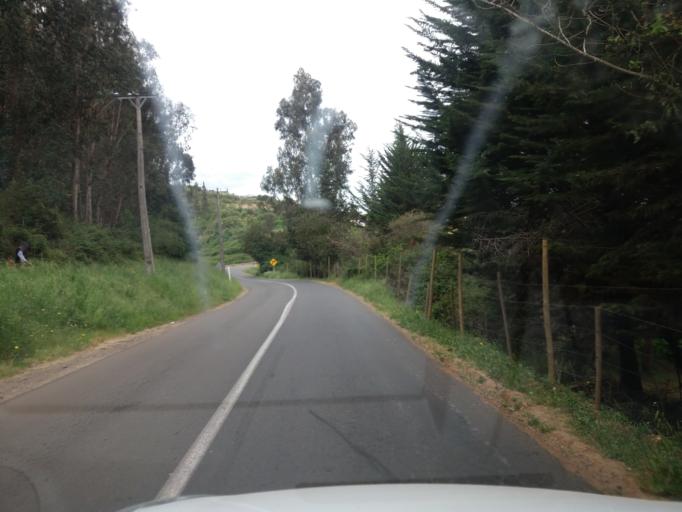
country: CL
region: Valparaiso
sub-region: Provincia de Marga Marga
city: Quilpue
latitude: -32.9176
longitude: -71.4387
